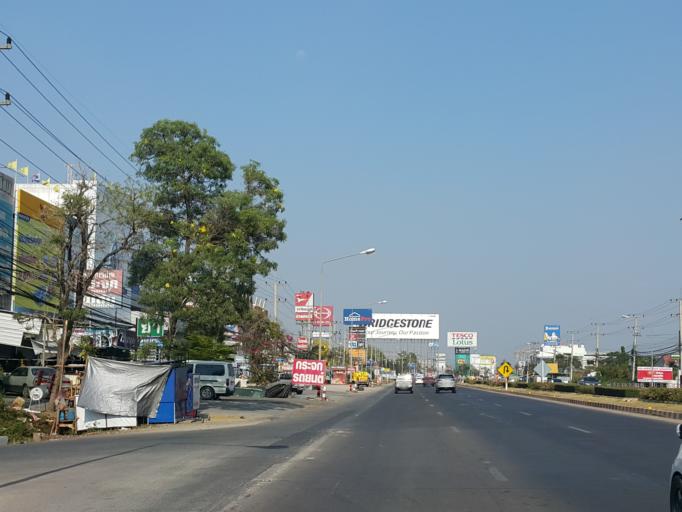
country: TH
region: Phitsanulok
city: Phitsanulok
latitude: 16.8181
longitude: 100.2941
